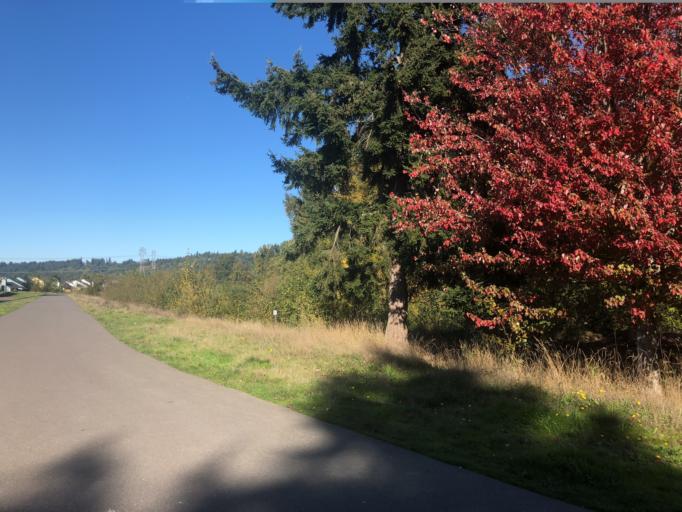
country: US
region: Washington
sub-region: King County
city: Auburn
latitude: 47.3323
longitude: -122.2133
